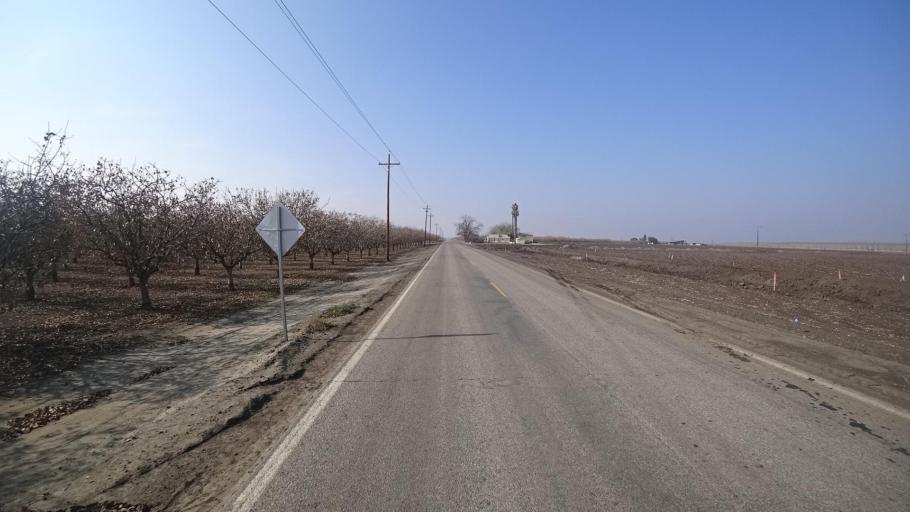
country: US
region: California
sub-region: Kern County
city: Buttonwillow
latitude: 35.3546
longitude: -119.4156
